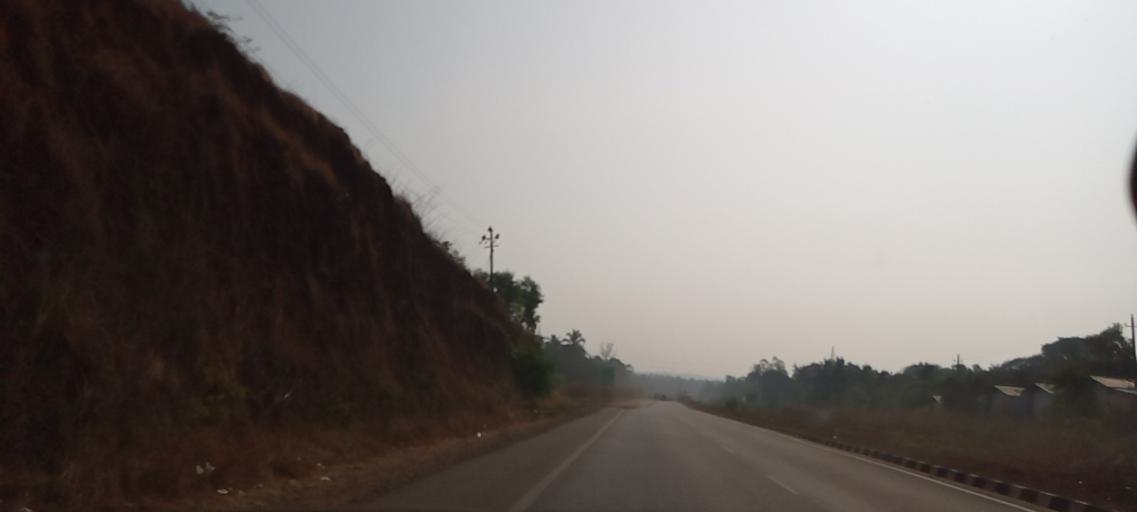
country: IN
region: Karnataka
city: Gangolli
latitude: 13.6886
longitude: 74.6709
